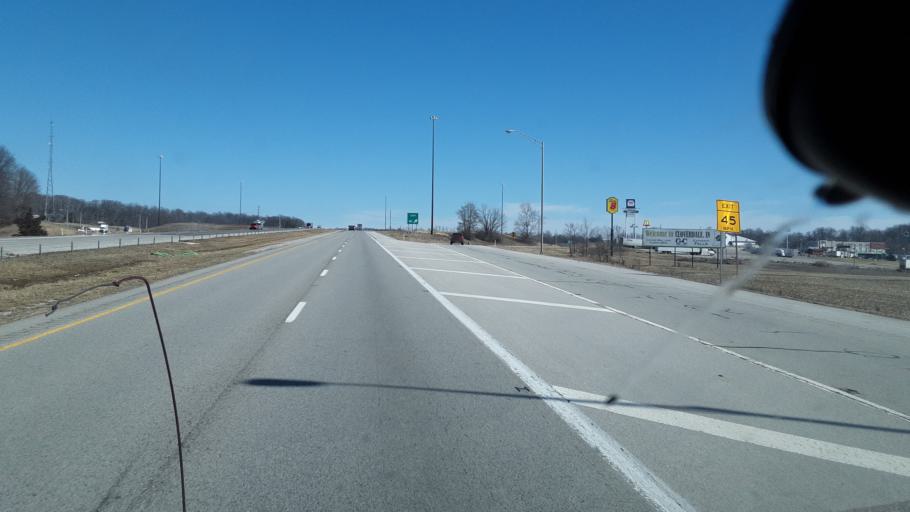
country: US
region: Indiana
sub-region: Putnam County
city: Cloverdale
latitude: 39.5324
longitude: -86.8082
